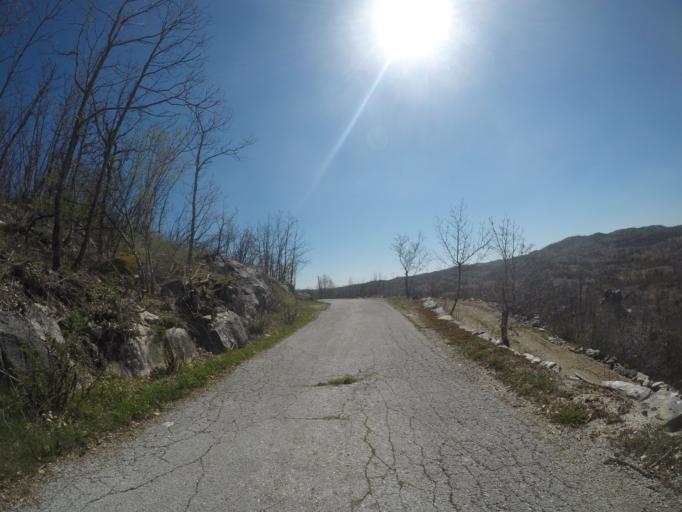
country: ME
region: Cetinje
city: Cetinje
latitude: 42.5284
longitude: 18.9666
